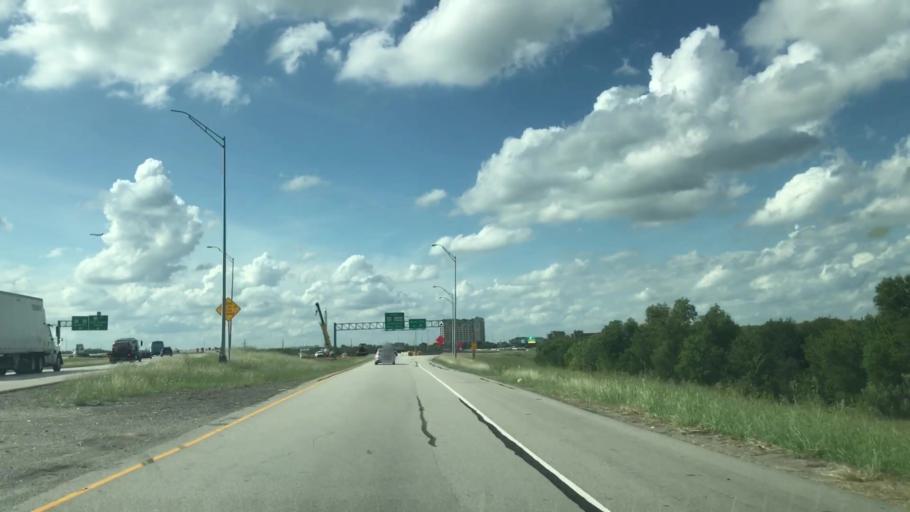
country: US
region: Texas
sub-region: Dallas County
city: Coppell
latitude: 32.9503
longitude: -97.0348
